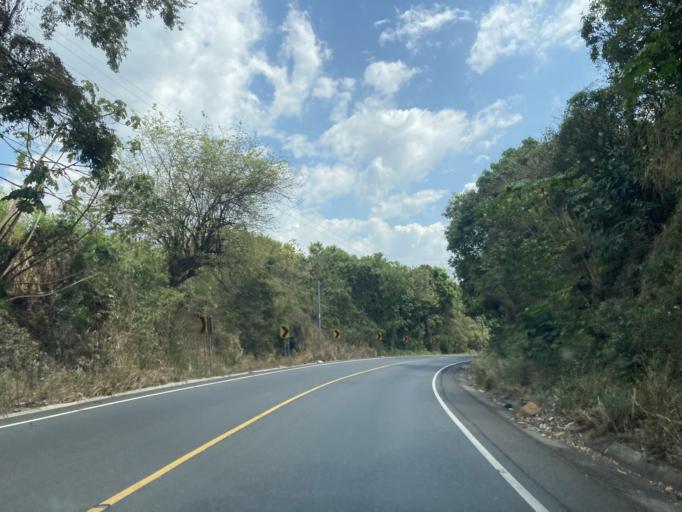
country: GT
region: Santa Rosa
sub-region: Municipio de Taxisco
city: Taxisco
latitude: 14.0653
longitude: -90.4575
